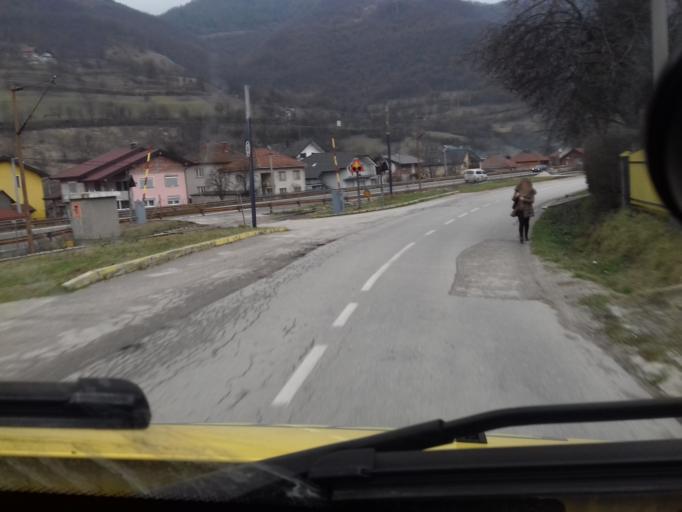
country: BA
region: Federation of Bosnia and Herzegovina
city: Zenica
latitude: 44.1530
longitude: 17.9621
